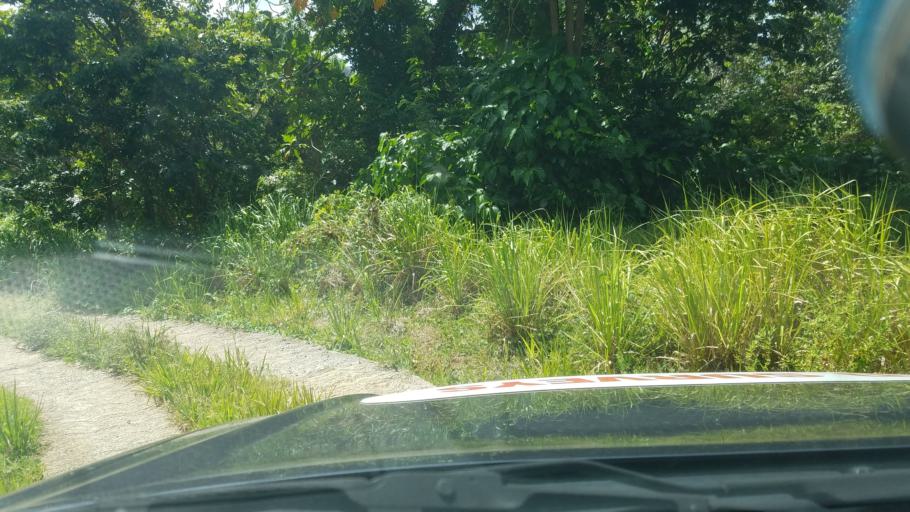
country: LC
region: Castries Quarter
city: Bisee
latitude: 14.0247
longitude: -60.9486
